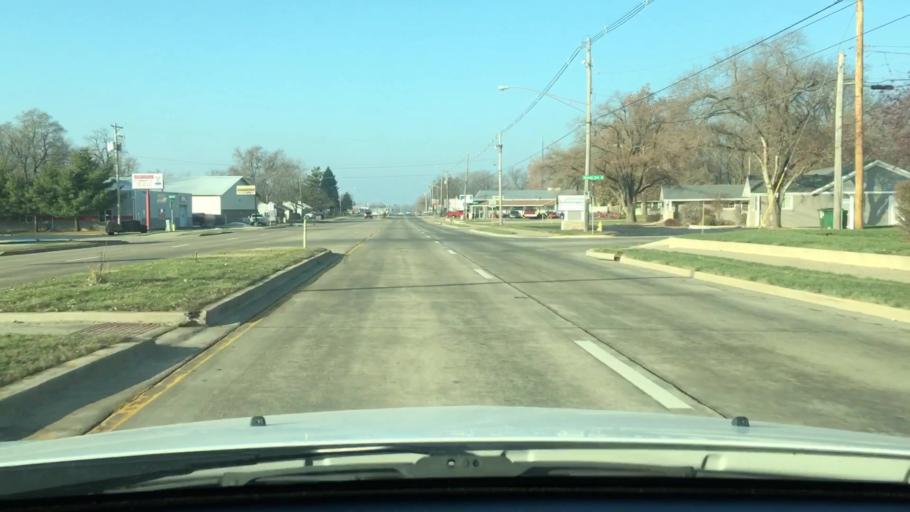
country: US
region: Illinois
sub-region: Woodford County
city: Germantown Hills
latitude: 40.6922
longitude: -89.4889
